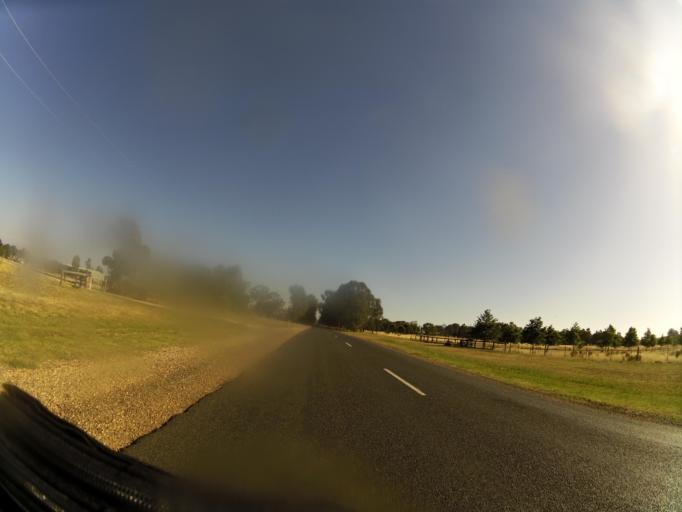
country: AU
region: Victoria
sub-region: Murrindindi
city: Kinglake West
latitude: -36.9867
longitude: 145.1117
